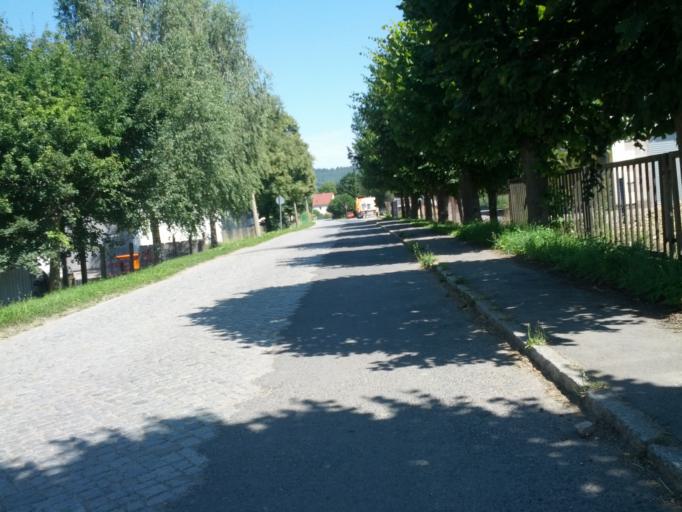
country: DE
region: Thuringia
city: Mihla
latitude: 51.0778
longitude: 10.3225
